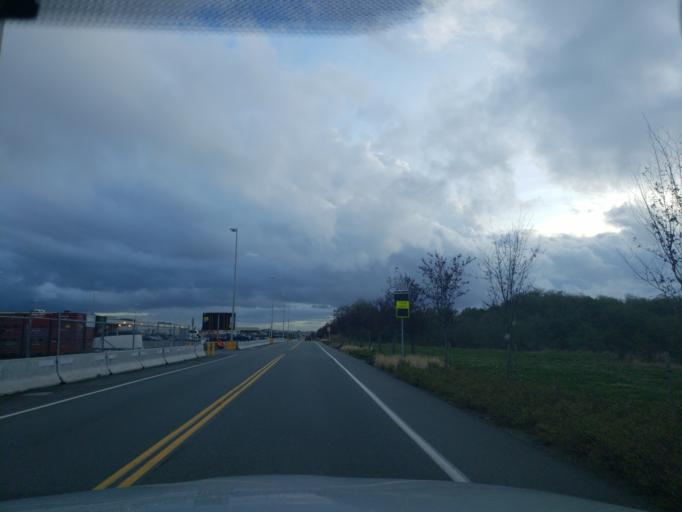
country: US
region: Washington
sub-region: Snohomish County
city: Mukilteo
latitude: 47.9331
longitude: -122.2848
